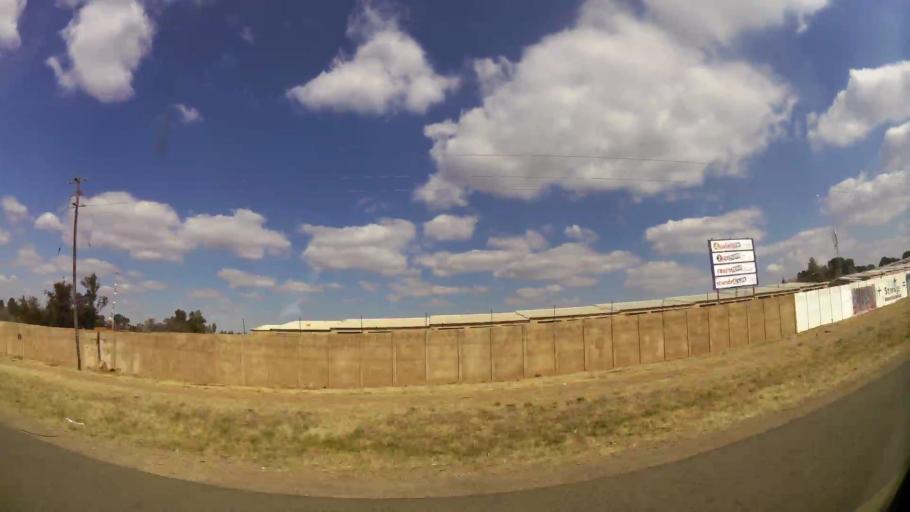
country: ZA
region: Gauteng
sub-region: City of Tshwane Metropolitan Municipality
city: Pretoria
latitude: -25.7410
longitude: 28.3389
